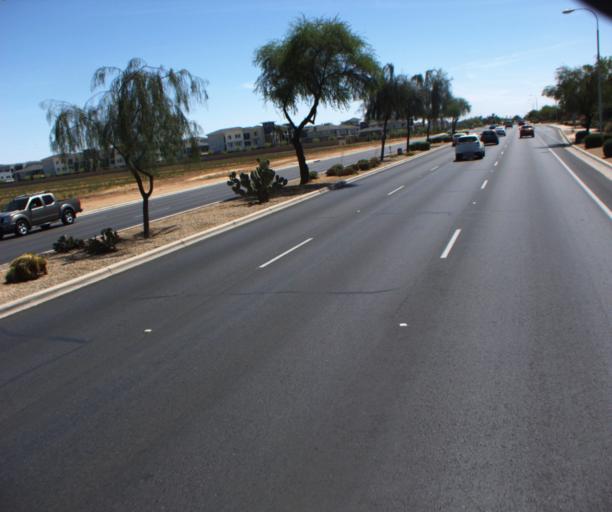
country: US
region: Arizona
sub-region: Maricopa County
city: Chandler
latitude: 33.2677
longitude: -111.8415
